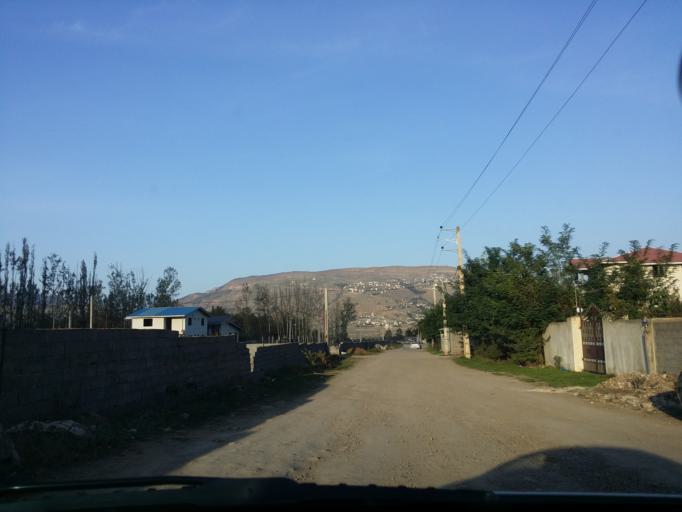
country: IR
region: Mazandaran
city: `Abbasabad
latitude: 36.5104
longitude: 51.1879
